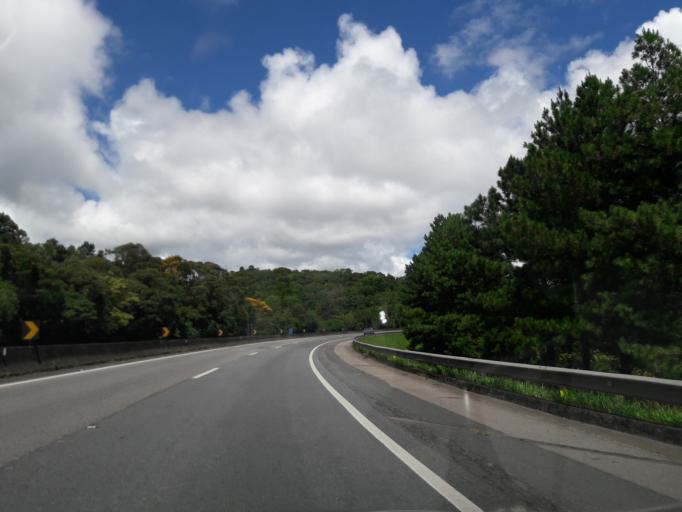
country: BR
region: Parana
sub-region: Campina Grande Do Sul
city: Campina Grande do Sul
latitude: -25.1740
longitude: -48.8684
